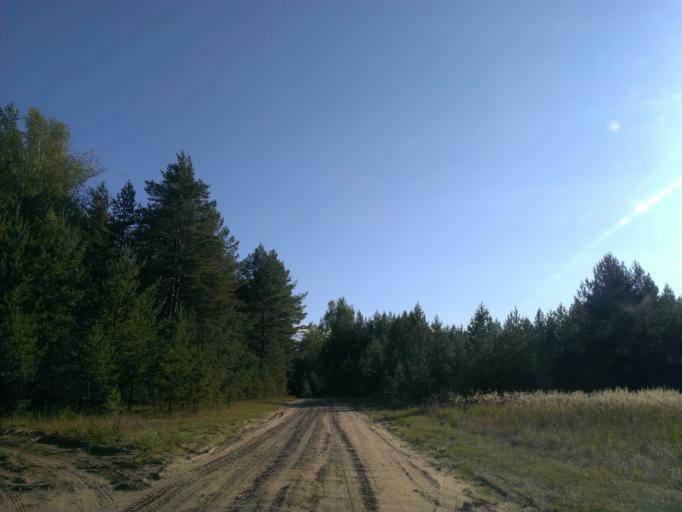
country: LV
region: Adazi
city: Adazi
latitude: 57.0546
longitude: 24.2555
